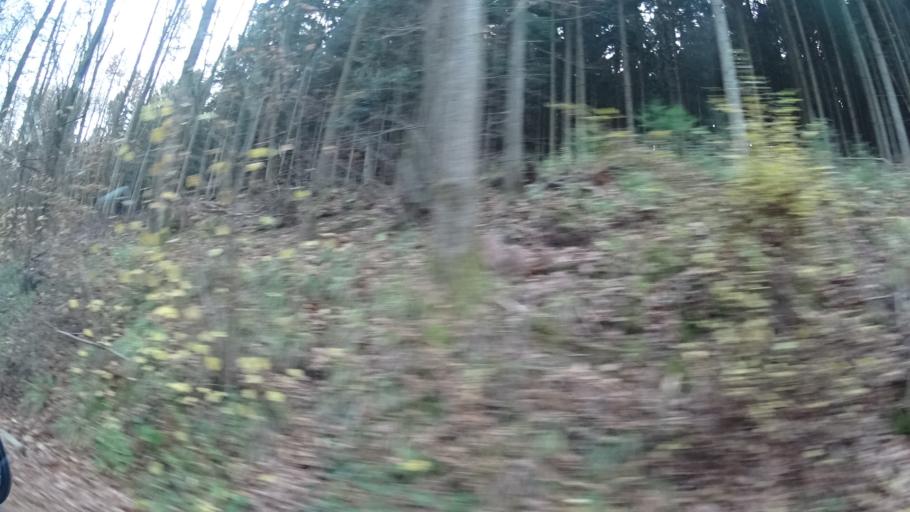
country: DE
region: Baden-Wuerttemberg
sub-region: Karlsruhe Region
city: Zwingenberg
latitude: 49.4125
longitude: 9.0236
